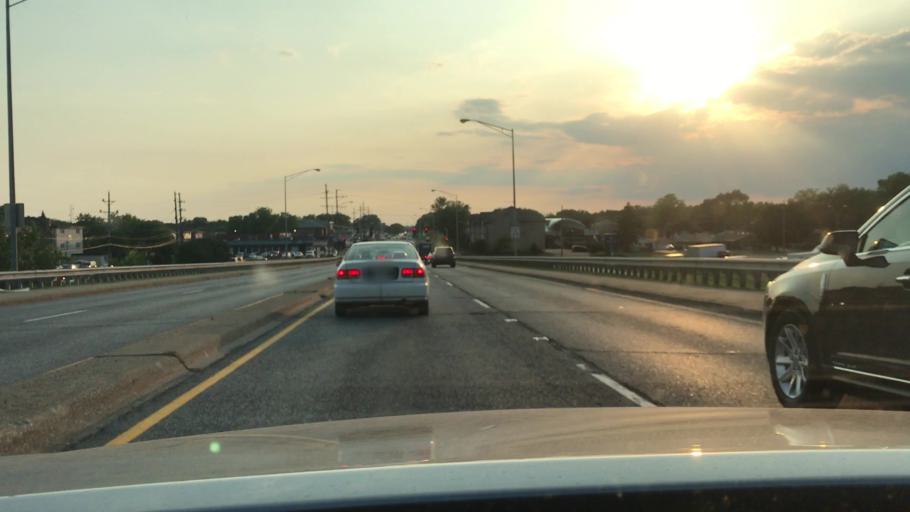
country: US
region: Illinois
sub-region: Cook County
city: Bridgeview
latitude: 41.7479
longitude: -87.8118
